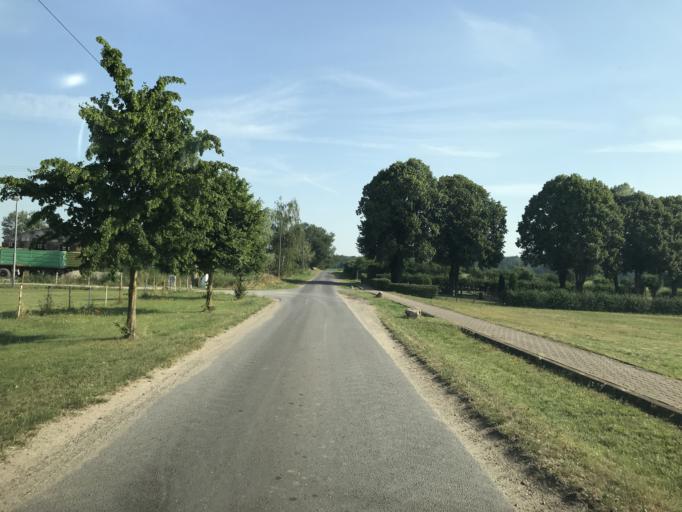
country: DE
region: Saxony-Anhalt
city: Beendorf
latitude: 52.2445
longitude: 11.1342
